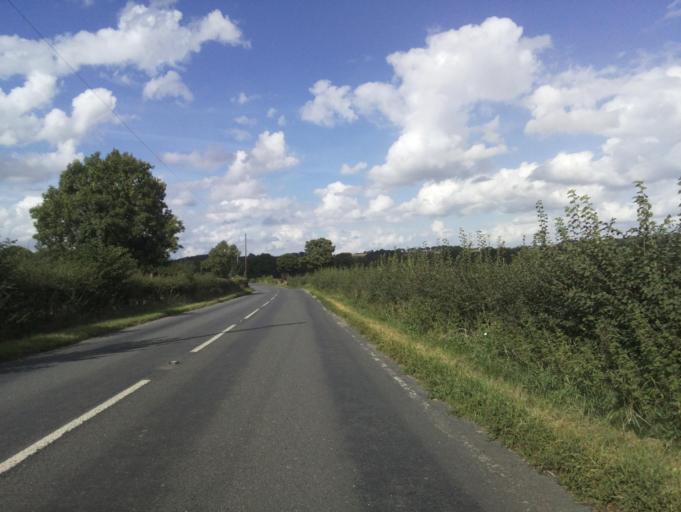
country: GB
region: England
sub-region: North Yorkshire
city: Leyburn
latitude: 54.2743
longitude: -1.7792
